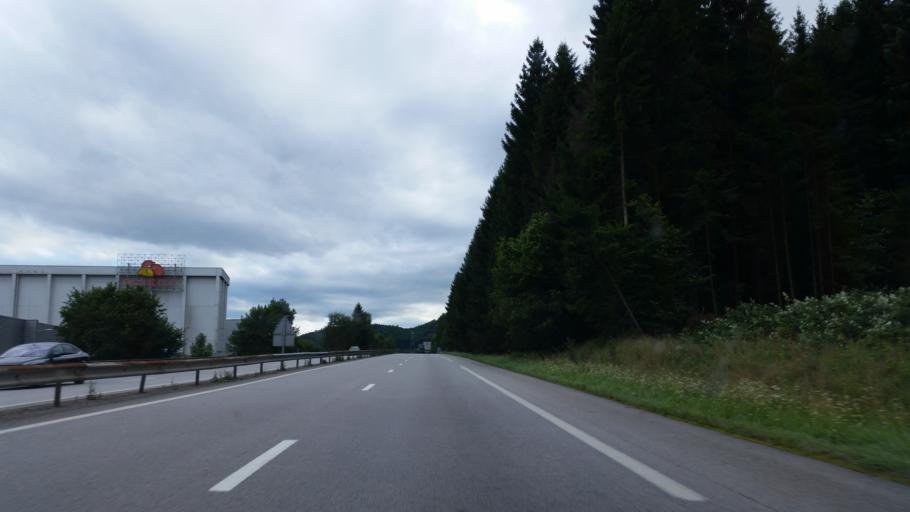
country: FR
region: Lorraine
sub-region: Departement des Vosges
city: Eloyes
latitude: 48.0865
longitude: 6.5969
